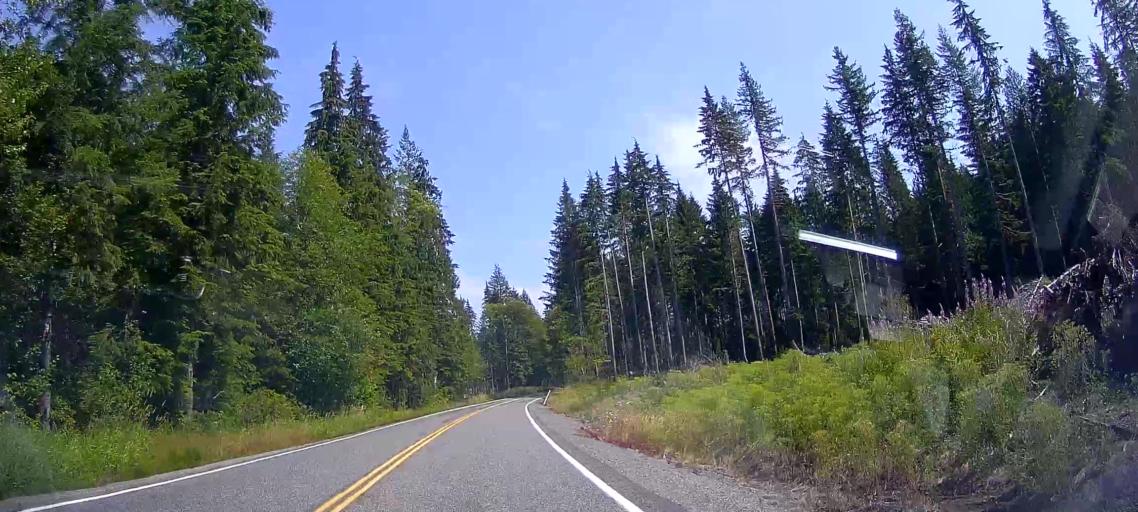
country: US
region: Washington
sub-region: Snohomish County
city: Bryant
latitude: 48.3448
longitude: -122.1008
